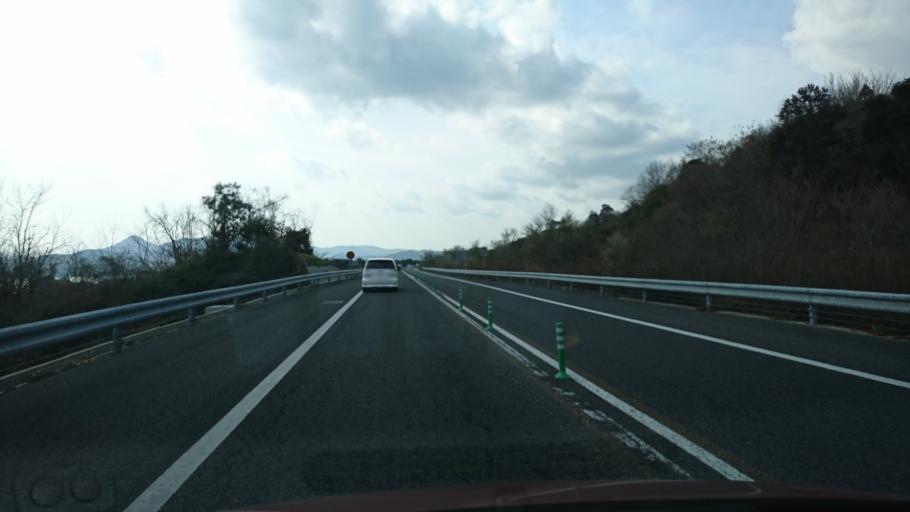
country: JP
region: Hiroshima
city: Innoshima
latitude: 34.2666
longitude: 133.0965
